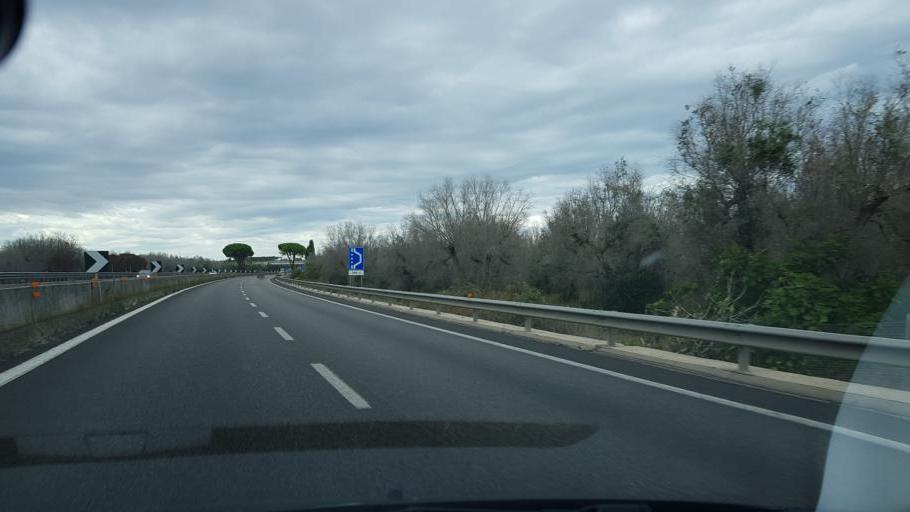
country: IT
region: Apulia
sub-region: Provincia di Lecce
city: Squinzano
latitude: 40.4523
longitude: 18.0663
